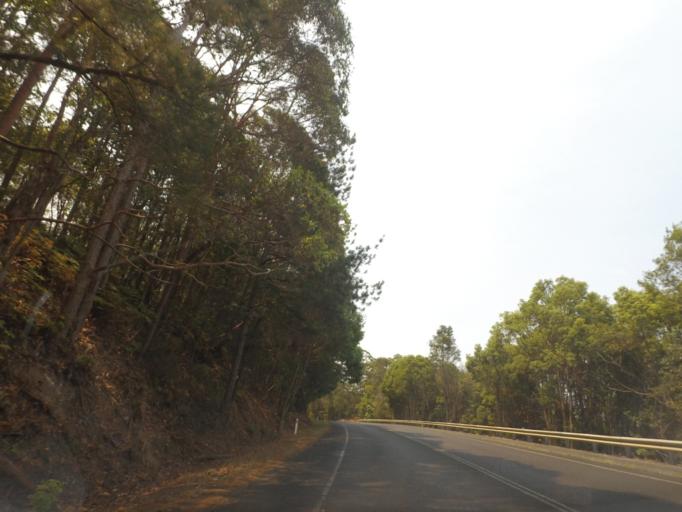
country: AU
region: New South Wales
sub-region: Byron Shire
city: Brunswick Heads
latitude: -28.5105
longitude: 153.5320
